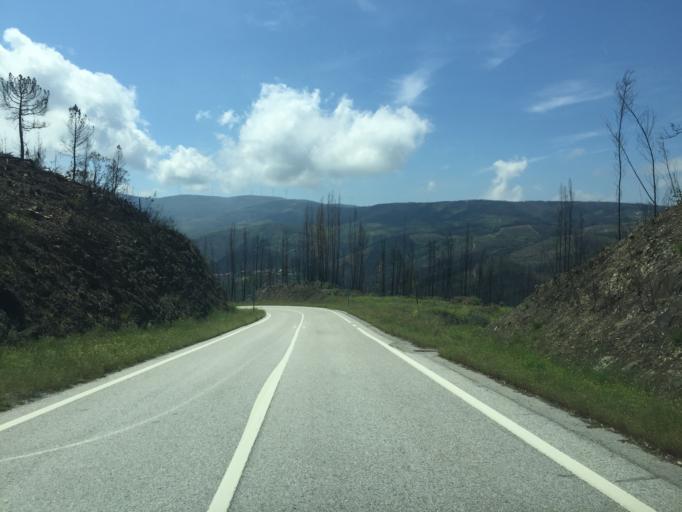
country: PT
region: Coimbra
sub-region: Pampilhosa da Serra
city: Pampilhosa da Serra
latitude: 39.9914
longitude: -7.9694
